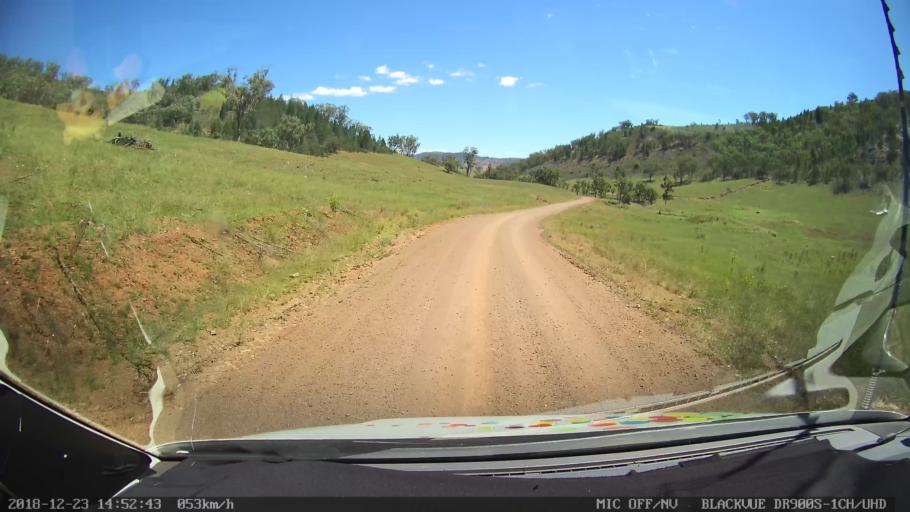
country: AU
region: New South Wales
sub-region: Tamworth Municipality
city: Manilla
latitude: -30.6861
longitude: 150.8538
